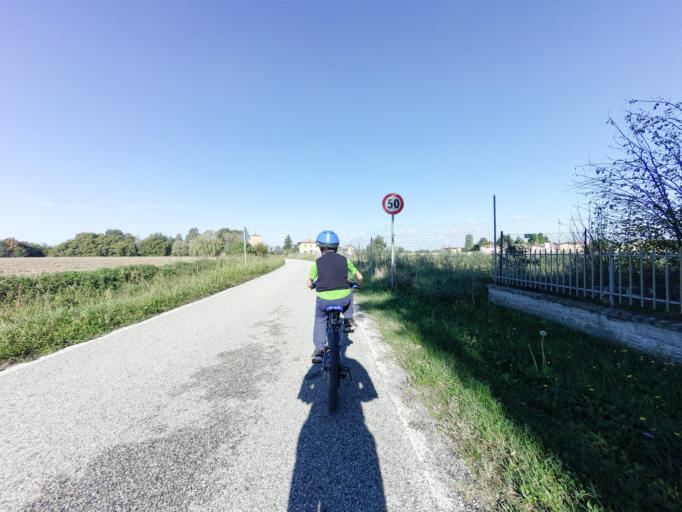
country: IT
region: Emilia-Romagna
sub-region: Provincia di Bologna
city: Bentivoglio
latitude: 44.5959
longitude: 11.4132
